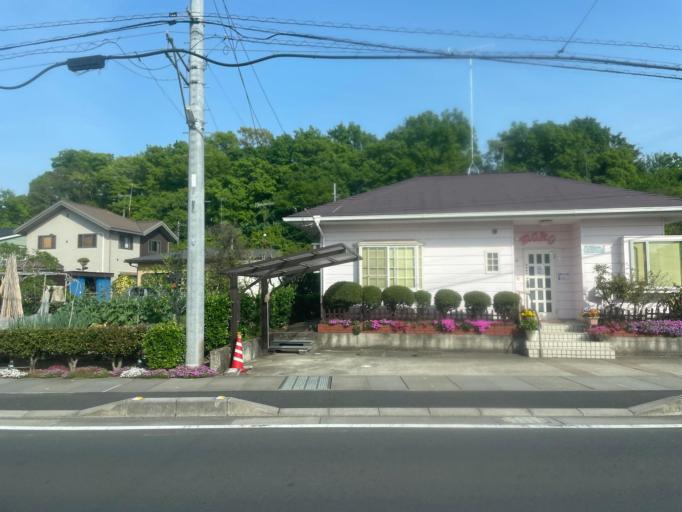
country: JP
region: Tochigi
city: Ashikaga
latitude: 36.3218
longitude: 139.4983
